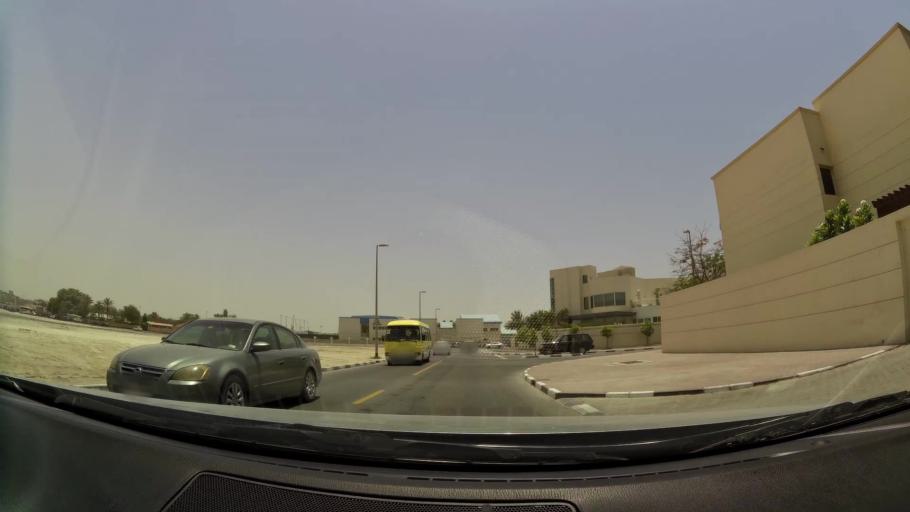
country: AE
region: Dubai
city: Dubai
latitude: 25.1823
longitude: 55.2428
